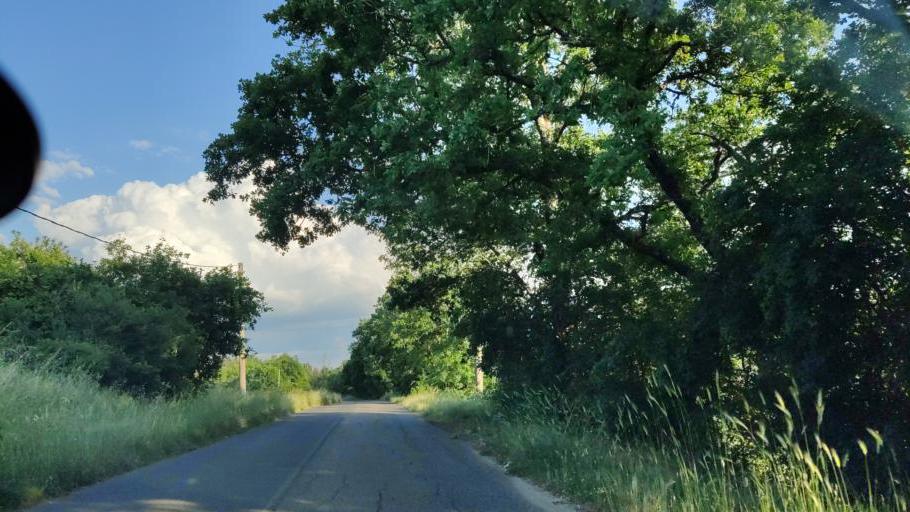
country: IT
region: Umbria
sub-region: Provincia di Terni
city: Lugnano in Teverina
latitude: 42.5938
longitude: 12.3741
